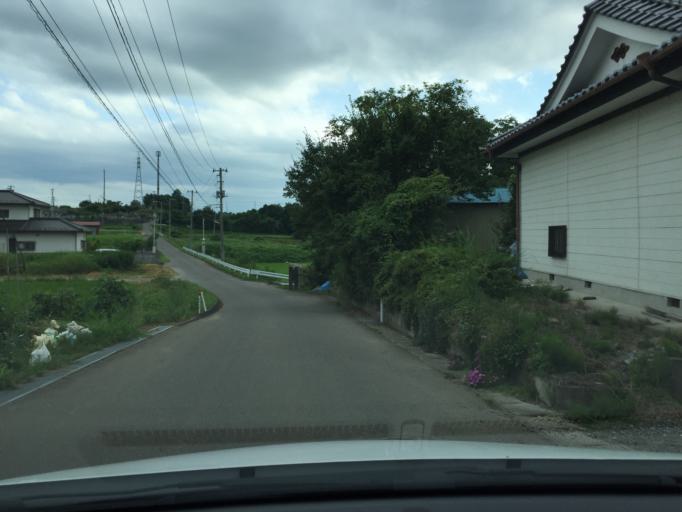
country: JP
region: Fukushima
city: Sukagawa
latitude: 37.2574
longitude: 140.3341
